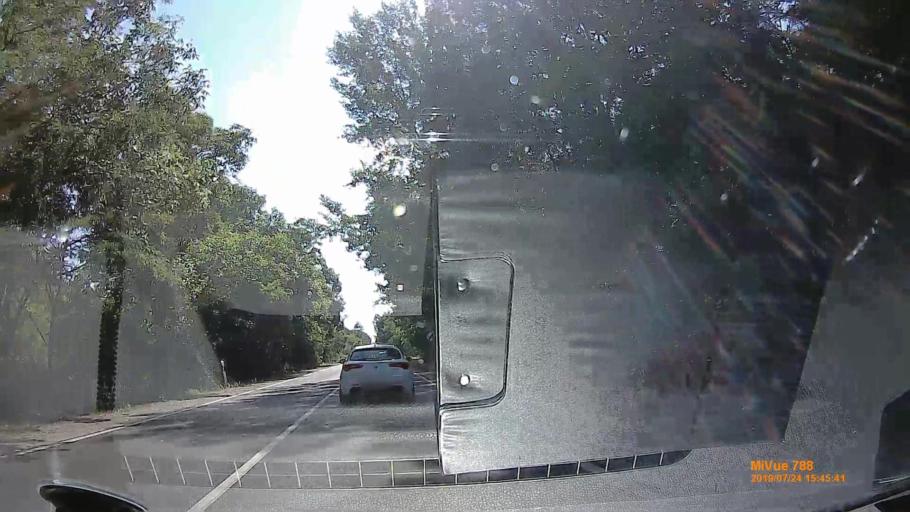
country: HU
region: Szabolcs-Szatmar-Bereg
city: Nagydobos
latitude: 48.0888
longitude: 22.2755
